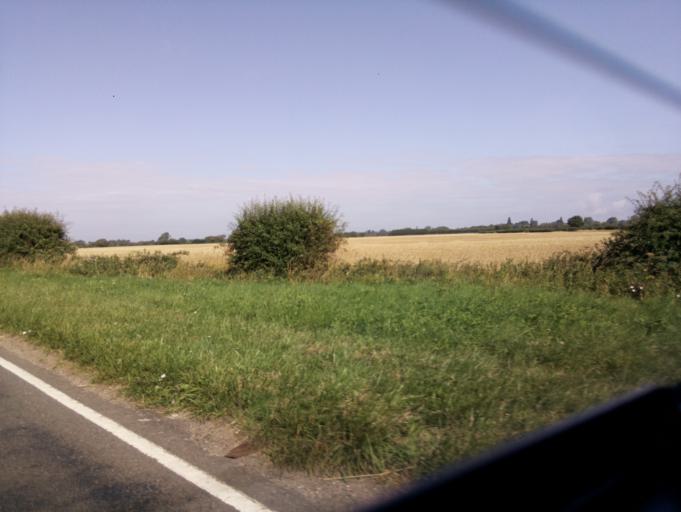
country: GB
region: England
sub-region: Oxfordshire
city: Bampton
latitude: 51.7222
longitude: -1.5671
